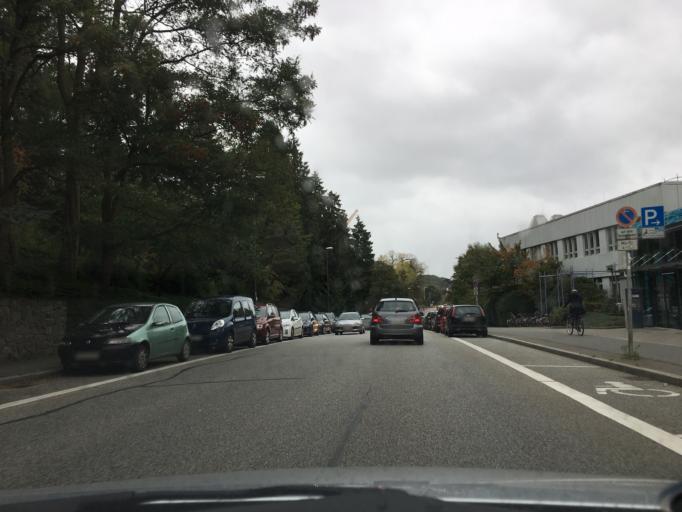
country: DE
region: Schleswig-Holstein
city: Kiel
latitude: 54.3298
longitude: 10.1478
